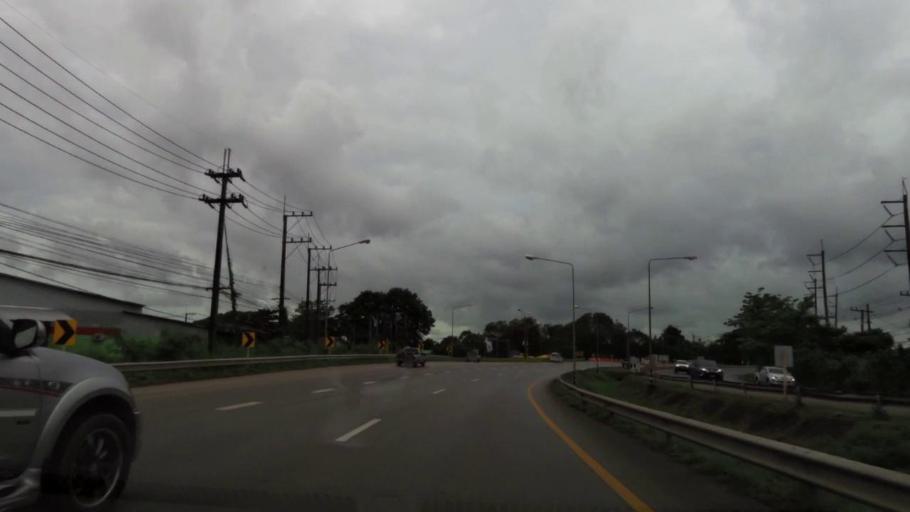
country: TH
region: Chanthaburi
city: Tha Mai
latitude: 12.6513
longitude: 102.0129
